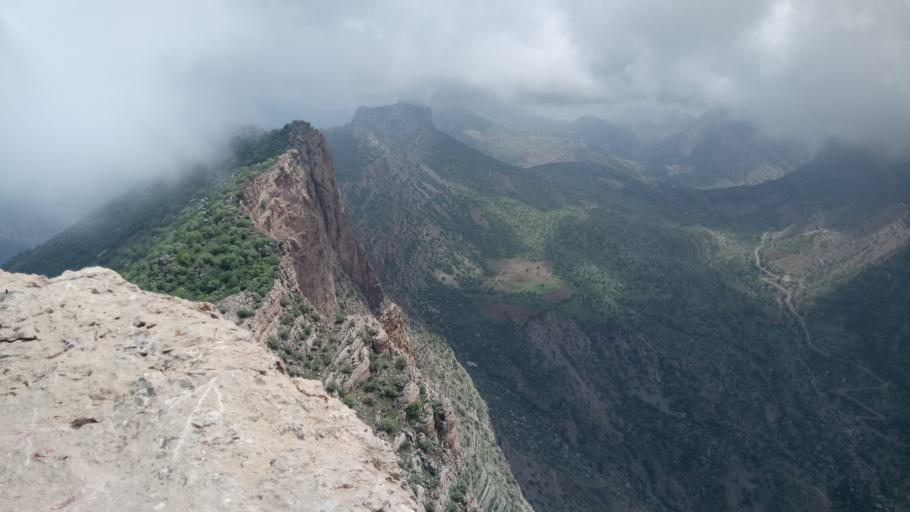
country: IQ
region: As Sulaymaniyah
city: Dukan
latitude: 35.9146
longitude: 45.0227
